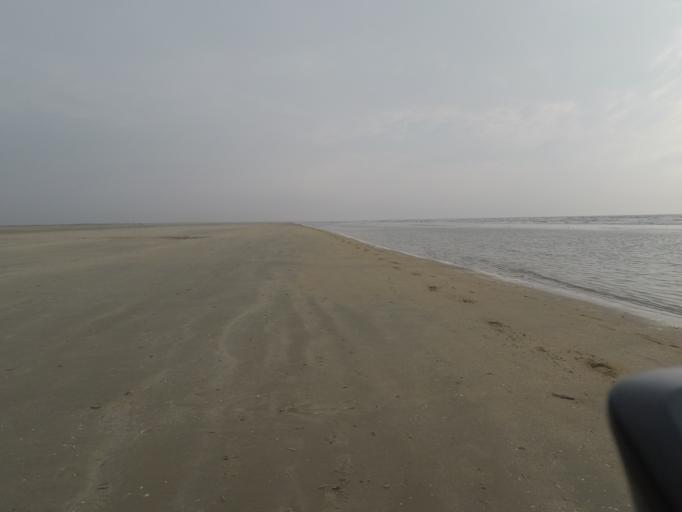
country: DE
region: Schleswig-Holstein
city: List
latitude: 55.1597
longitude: 8.4763
